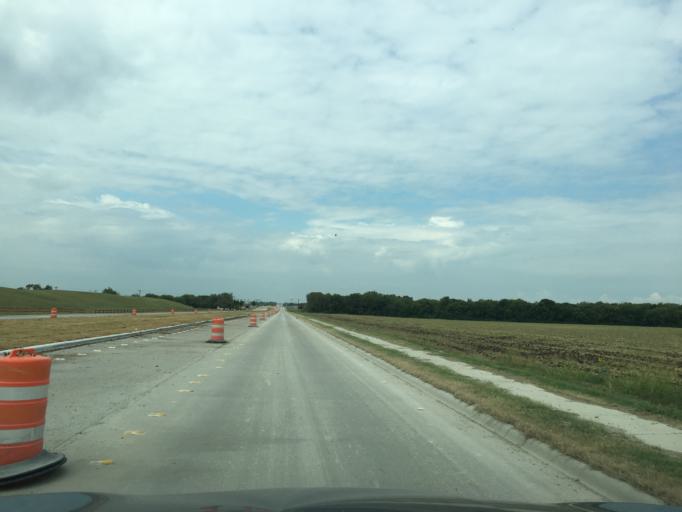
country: US
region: Texas
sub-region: Collin County
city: Melissa
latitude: 33.2994
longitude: -96.5346
